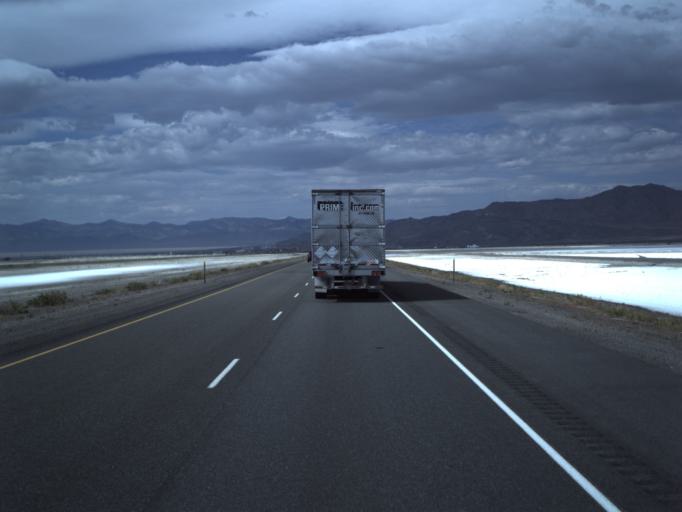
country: US
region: Utah
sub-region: Tooele County
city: Wendover
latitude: 40.7410
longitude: -113.9327
